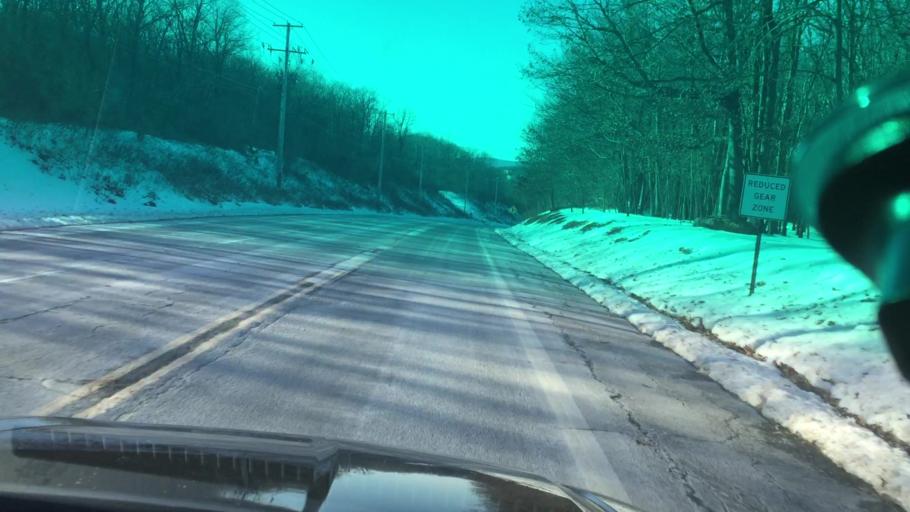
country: US
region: Pennsylvania
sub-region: Luzerne County
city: Oakdale
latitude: 41.0175
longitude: -75.9250
